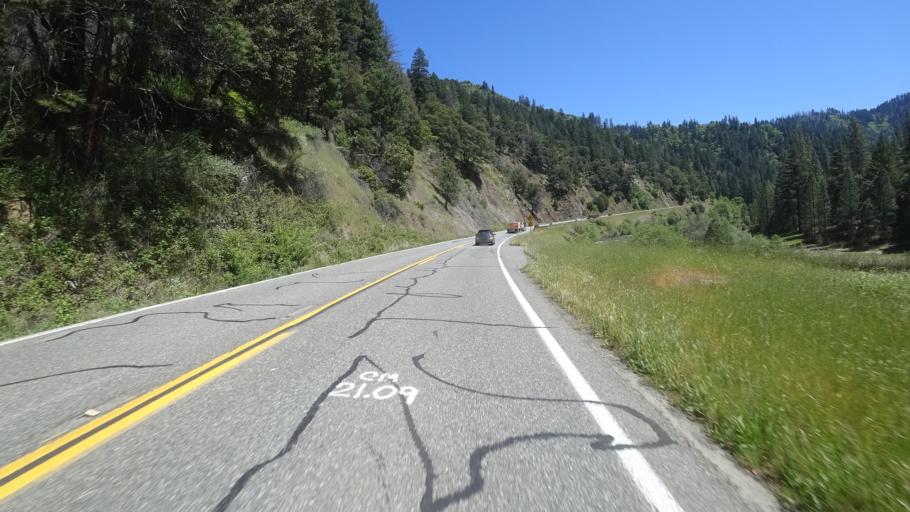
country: US
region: California
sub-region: Trinity County
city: Hayfork
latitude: 40.7850
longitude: -123.3390
